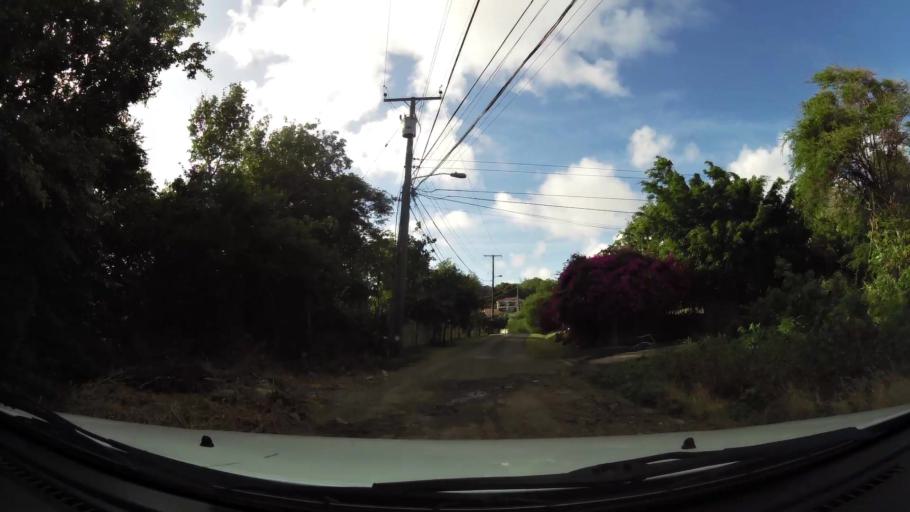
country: LC
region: Gros-Islet
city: Gros Islet
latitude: 14.1001
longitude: -60.9403
